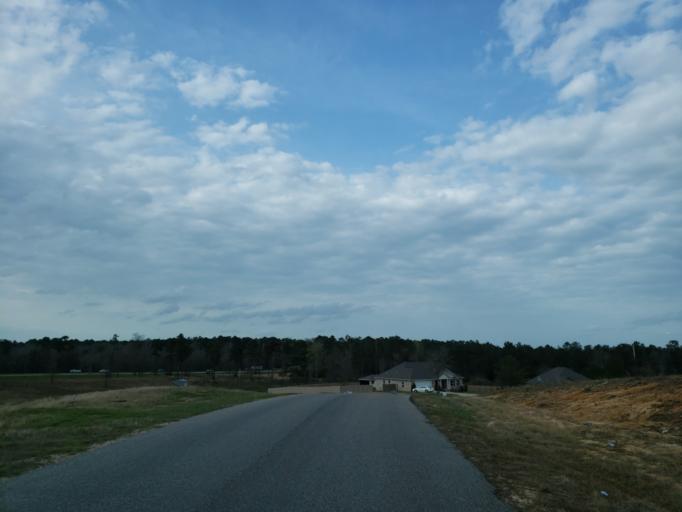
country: US
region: Mississippi
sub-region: Jones County
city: Ellisville
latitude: 31.5628
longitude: -89.2519
